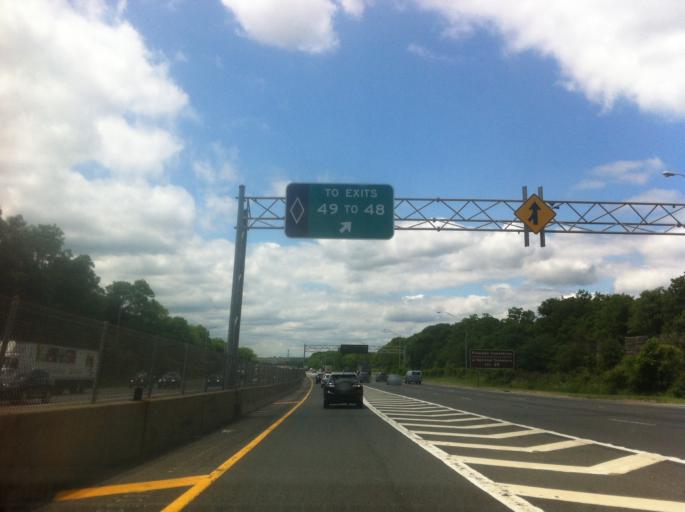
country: US
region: New York
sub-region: Suffolk County
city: Wheatley Heights
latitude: 40.7869
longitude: -73.3862
